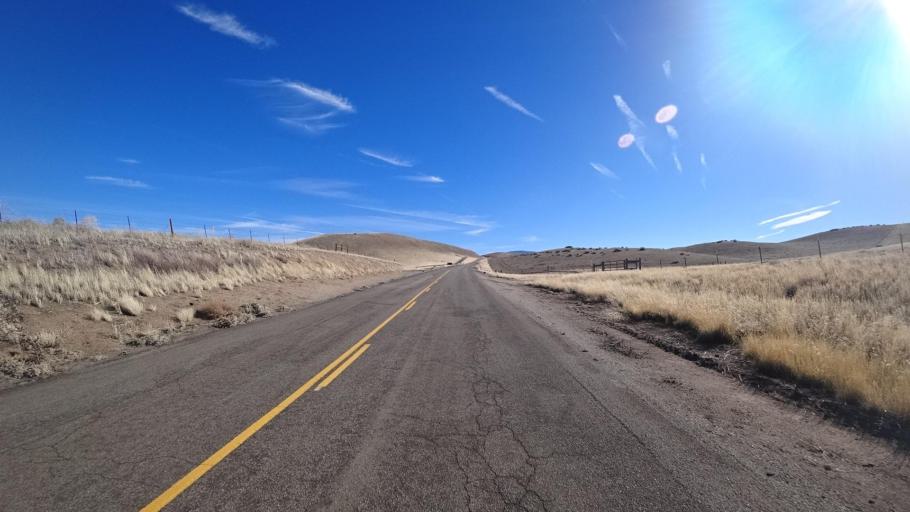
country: US
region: California
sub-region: Kern County
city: Maricopa
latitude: 34.9047
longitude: -119.3786
